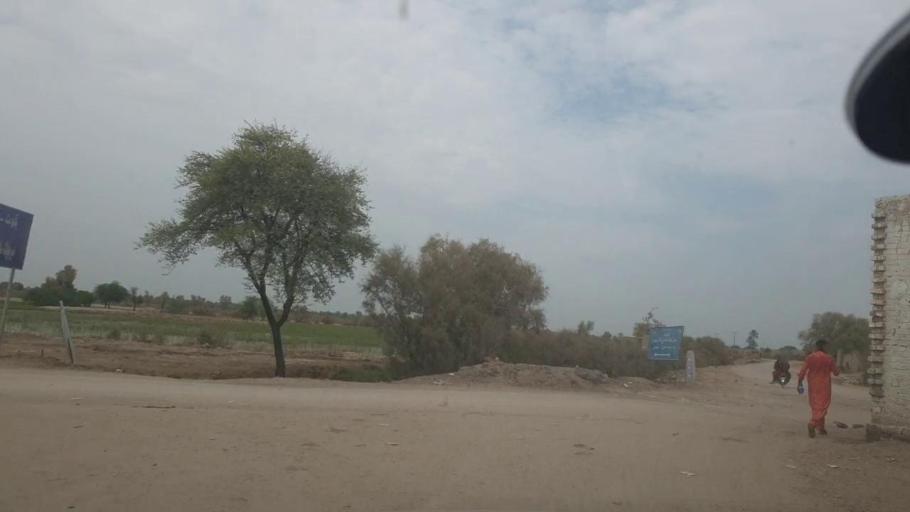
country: PK
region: Balochistan
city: Mehrabpur
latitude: 28.0594
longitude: 68.1515
